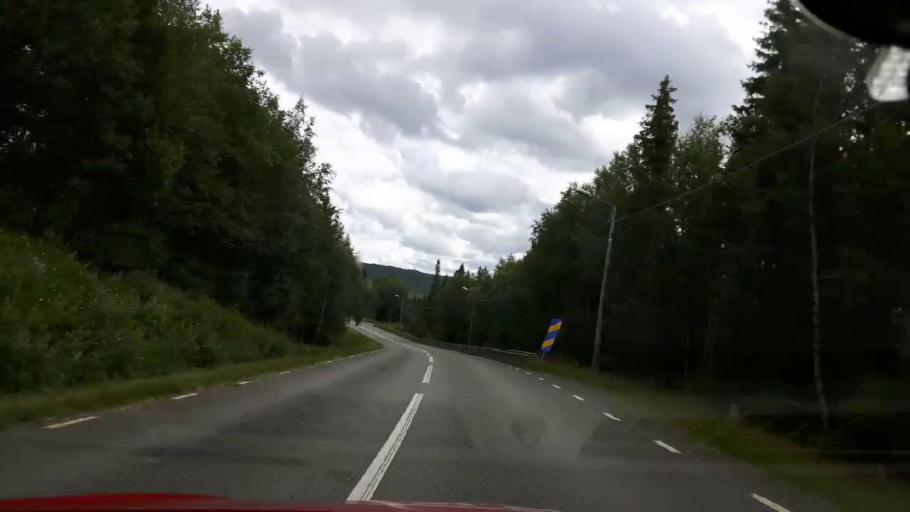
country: NO
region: Nord-Trondelag
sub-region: Lierne
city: Sandvika
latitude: 64.3915
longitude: 14.3722
